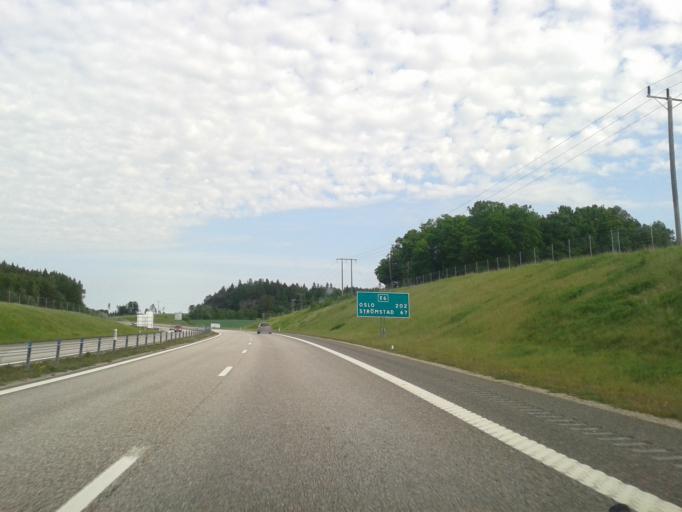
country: SE
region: Vaestra Goetaland
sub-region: Munkedals Kommun
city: Munkedal
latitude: 58.4706
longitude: 11.6498
